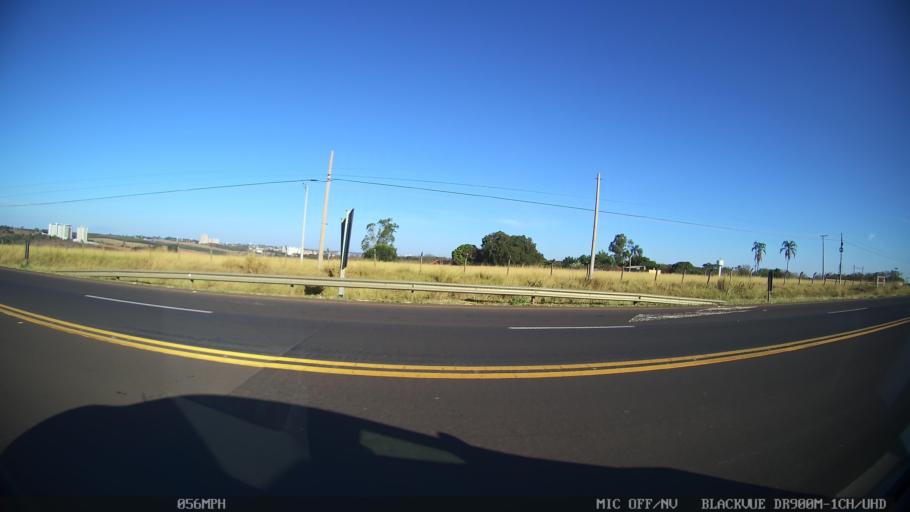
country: BR
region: Sao Paulo
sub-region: Olimpia
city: Olimpia
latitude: -20.6996
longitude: -48.9365
